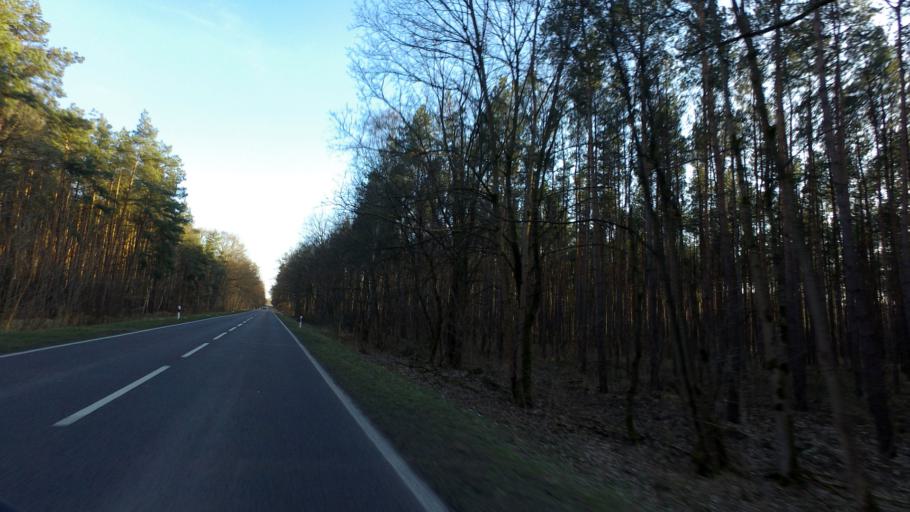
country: DE
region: Brandenburg
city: Eberswalde
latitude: 52.7972
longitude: 13.8366
